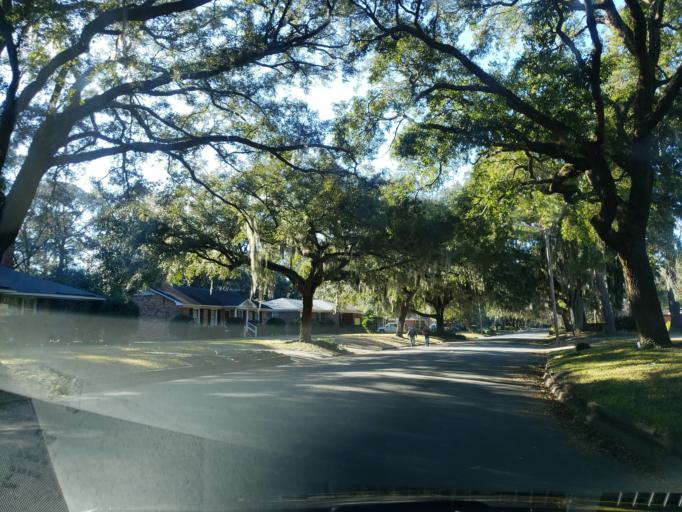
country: US
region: Georgia
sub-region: Chatham County
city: Thunderbolt
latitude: 32.0202
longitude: -81.0981
